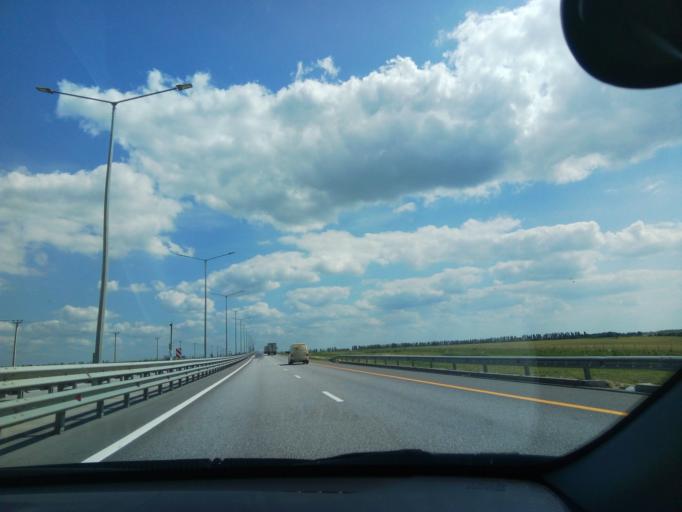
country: RU
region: Voronezj
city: Kashirskoye
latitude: 51.4919
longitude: 39.5296
